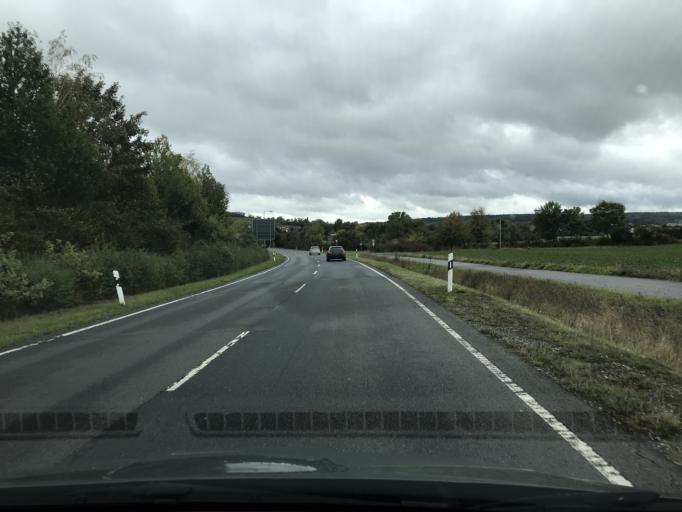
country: DE
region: Bavaria
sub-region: Regierungsbezirk Unterfranken
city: Grossostheim
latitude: 49.9188
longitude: 9.0585
